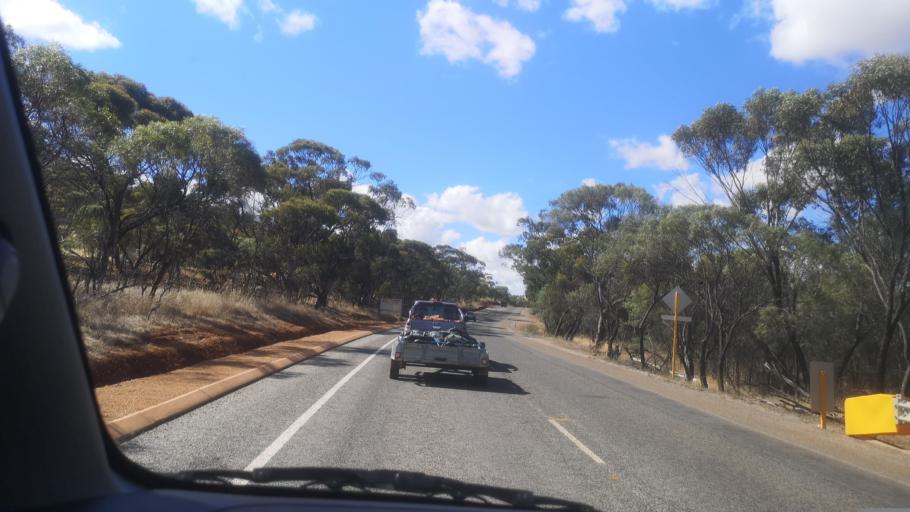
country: AU
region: Western Australia
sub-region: Toodyay
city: Toodyay
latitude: -31.5635
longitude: 116.4760
